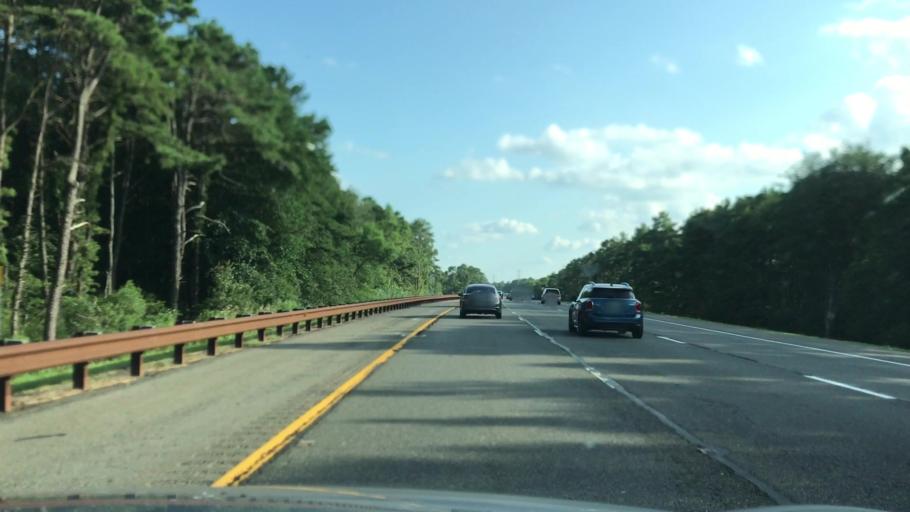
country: US
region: New Jersey
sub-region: Ocean County
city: Forked River
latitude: 39.8346
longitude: -74.2255
